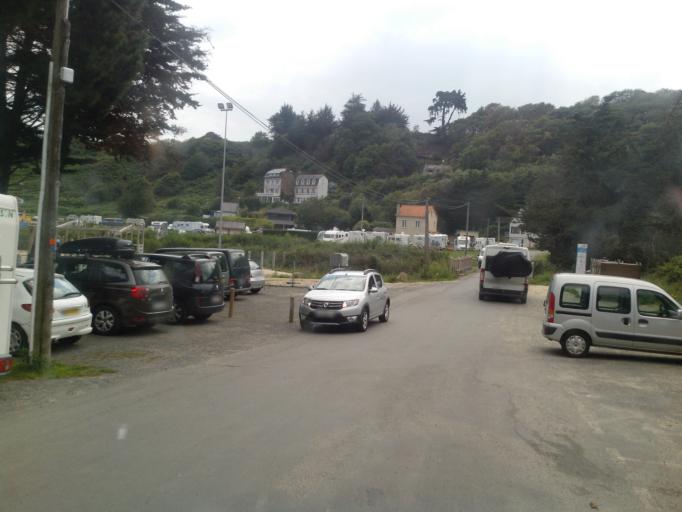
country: FR
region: Brittany
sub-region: Departement des Cotes-d'Armor
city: Plouha
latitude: 48.6772
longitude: -2.8855
